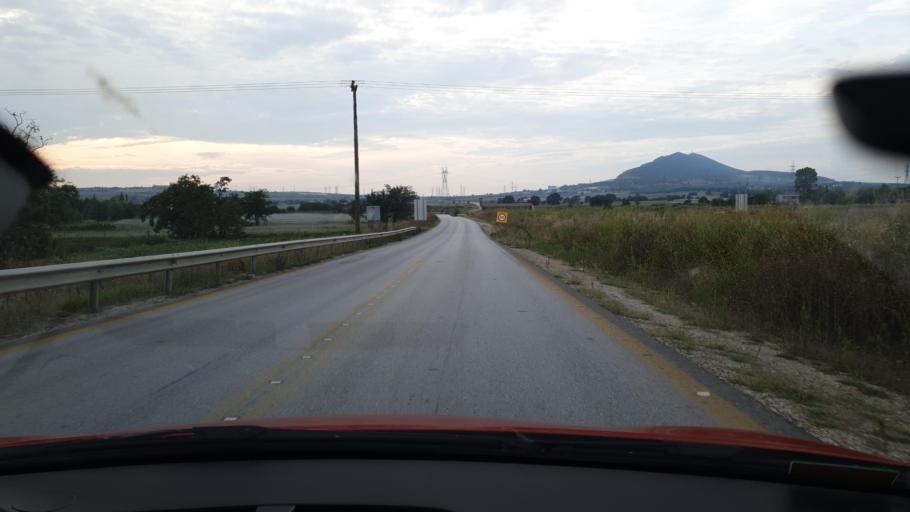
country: GR
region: Central Macedonia
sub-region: Nomos Thessalonikis
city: Assiros
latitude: 40.7857
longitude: 23.0089
